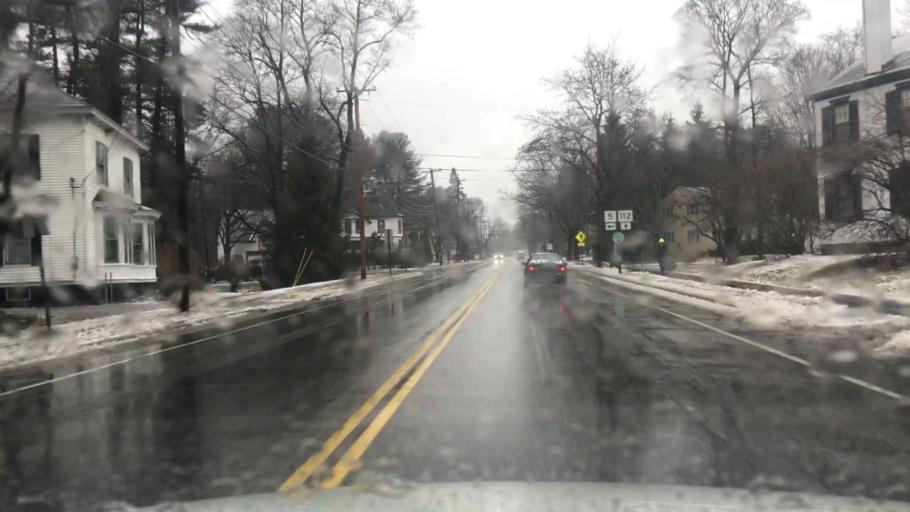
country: US
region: Maine
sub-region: York County
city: Saco
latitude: 43.5051
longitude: -70.4465
